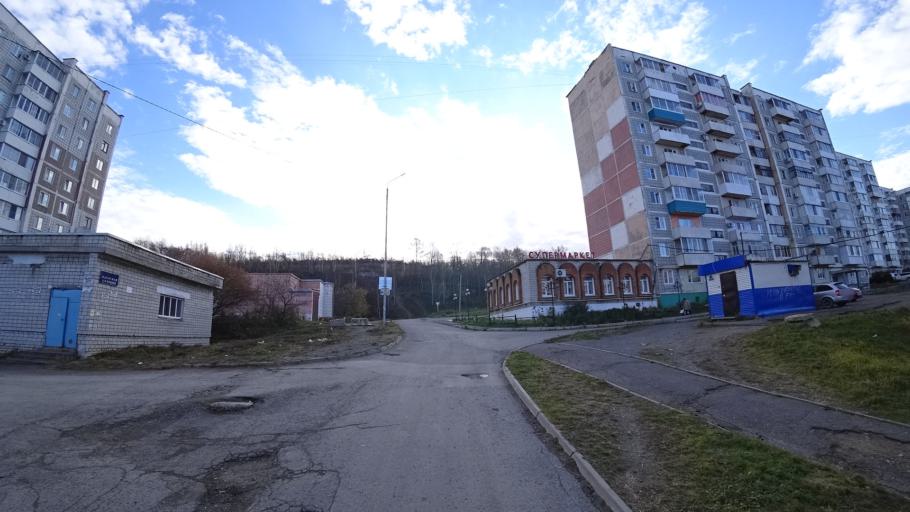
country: RU
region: Khabarovsk Krai
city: Amursk
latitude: 50.2460
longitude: 136.9205
